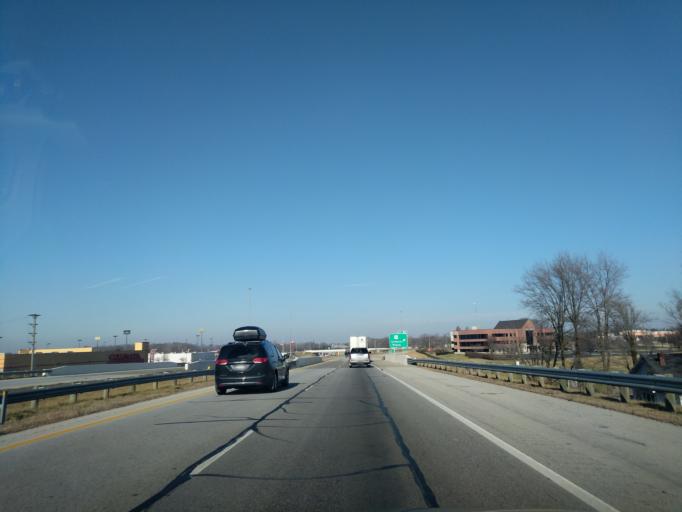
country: US
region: Ohio
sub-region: Miami County
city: Piqua
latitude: 40.1451
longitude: -84.2185
